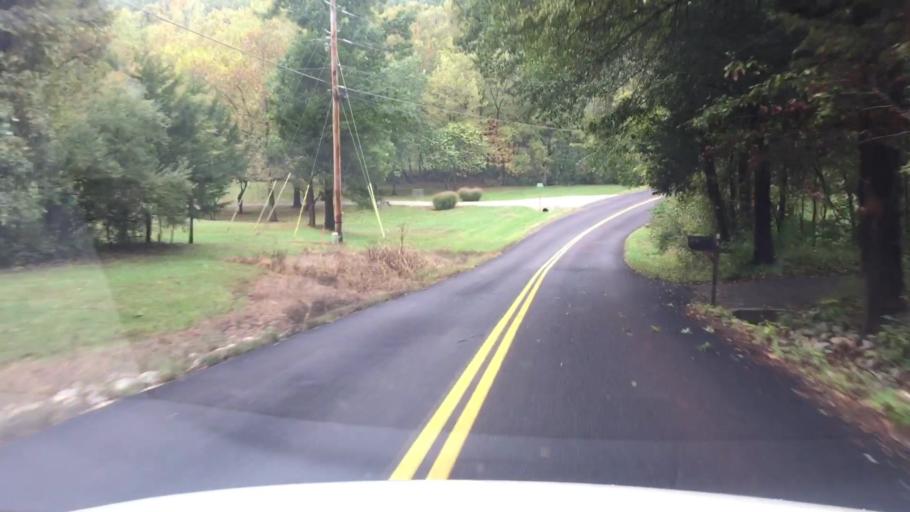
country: US
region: Missouri
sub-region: Boone County
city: Columbia
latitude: 38.8600
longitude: -92.3441
